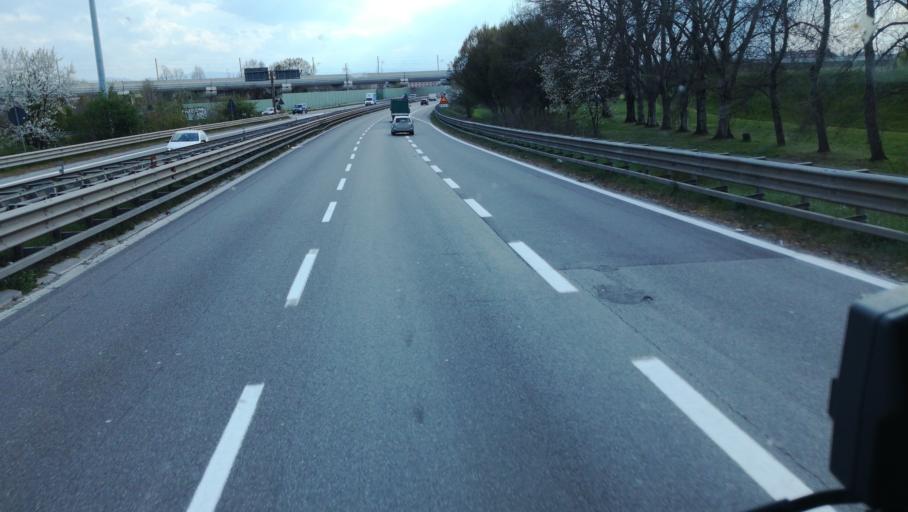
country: IT
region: Emilia-Romagna
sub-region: Provincia di Modena
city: Villanova
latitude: 44.6696
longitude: 10.9083
